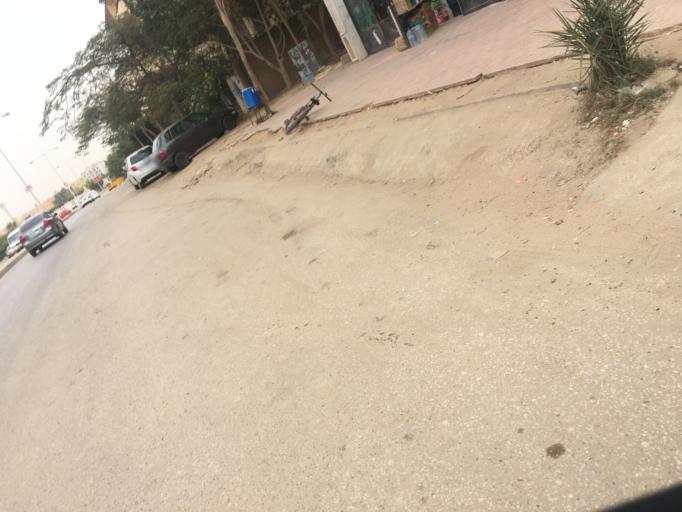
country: EG
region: Al Jizah
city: Madinat Sittah Uktubar
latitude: 29.9810
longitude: 30.9469
